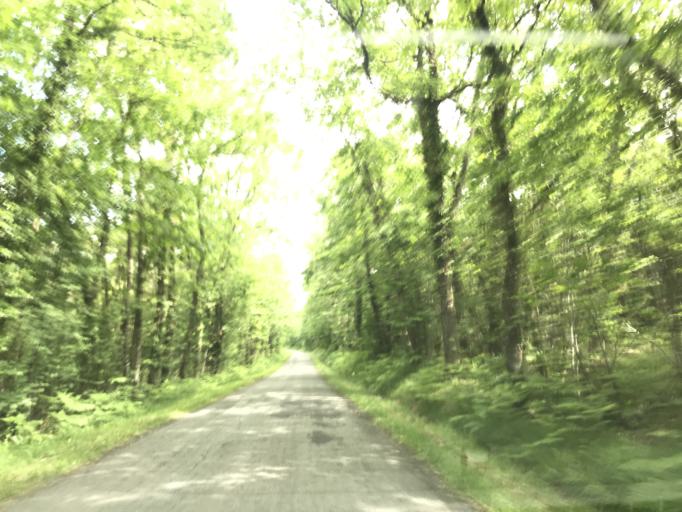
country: FR
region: Poitou-Charentes
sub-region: Departement de la Charente
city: Chalais
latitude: 45.2755
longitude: 0.1078
